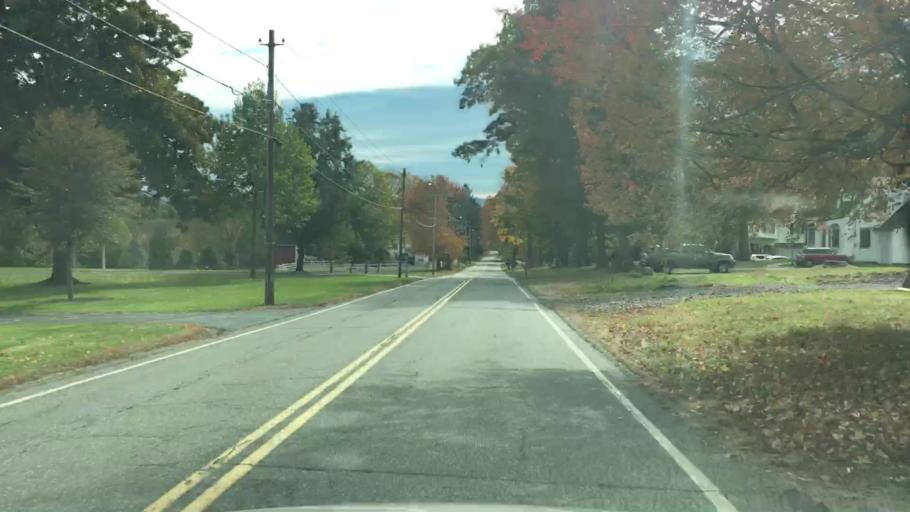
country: US
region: Massachusetts
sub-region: Hampden County
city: East Longmeadow
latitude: 42.0407
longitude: -72.4988
